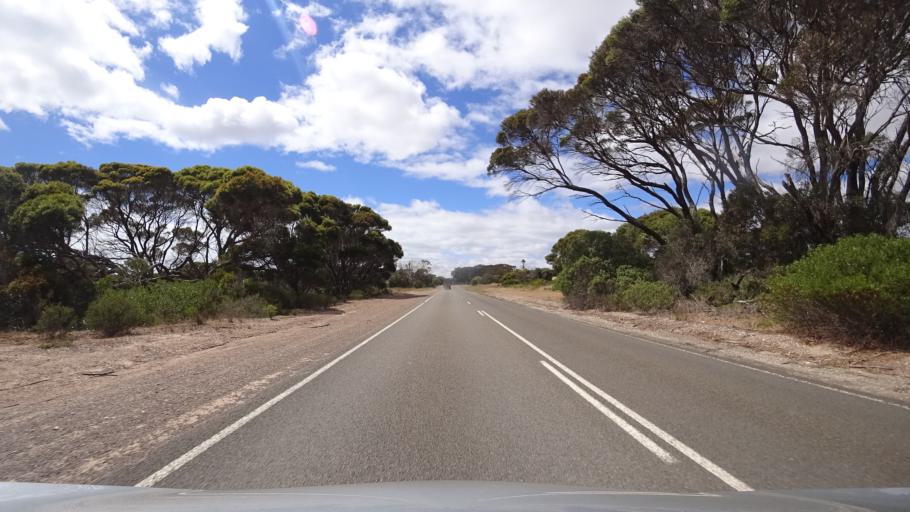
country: AU
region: South Australia
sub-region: Kangaroo Island
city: Kingscote
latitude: -35.6476
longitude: 137.5619
